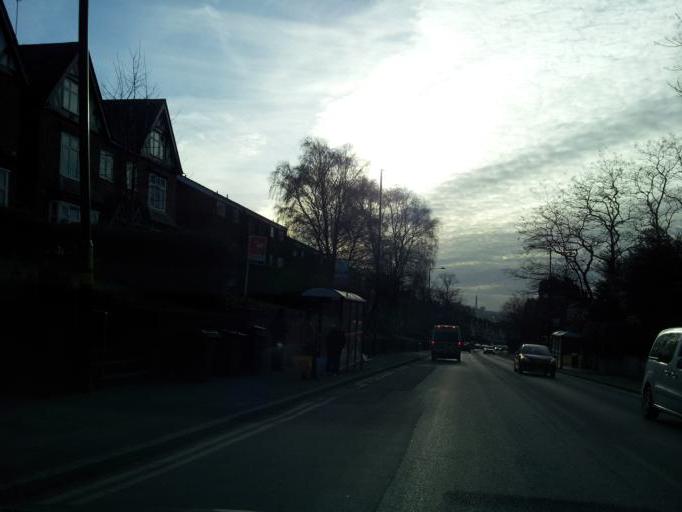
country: GB
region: England
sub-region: City and Borough of Birmingham
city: Birmingham
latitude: 52.5121
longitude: -1.8529
